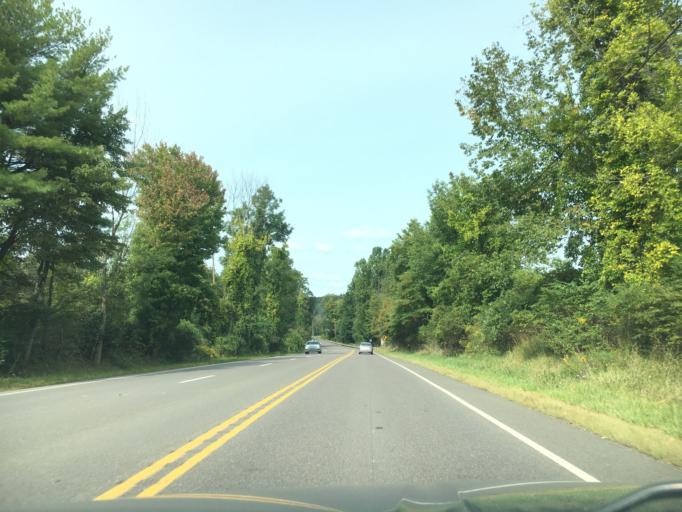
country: US
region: Pennsylvania
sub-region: Carbon County
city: Summit Hill
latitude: 40.7149
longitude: -75.8430
